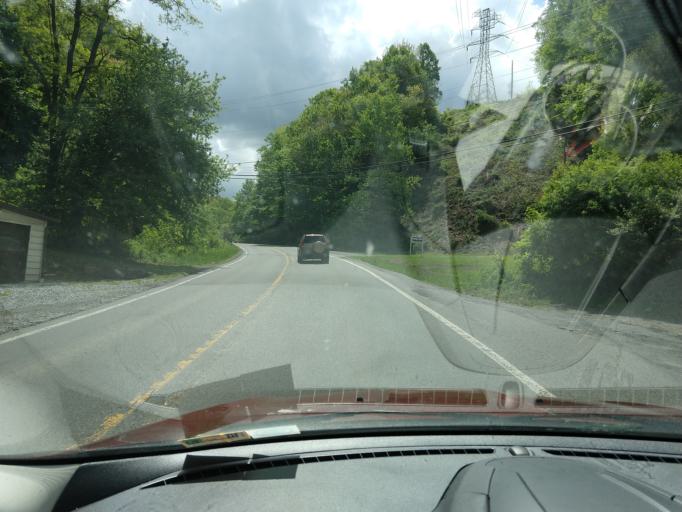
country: US
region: West Virginia
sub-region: Mercer County
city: Bluefield
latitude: 37.2616
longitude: -81.2368
